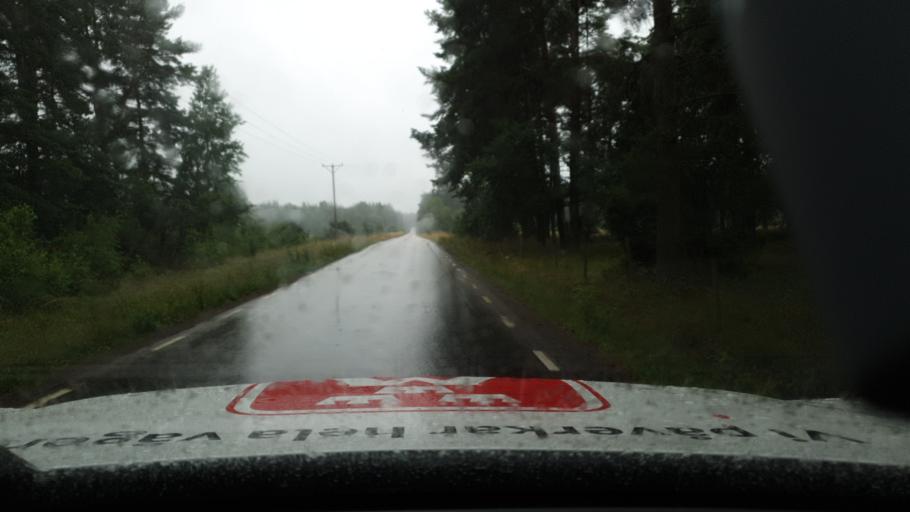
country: SE
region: Vaestra Goetaland
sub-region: Falkopings Kommun
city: Floby
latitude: 58.1818
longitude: 13.3462
